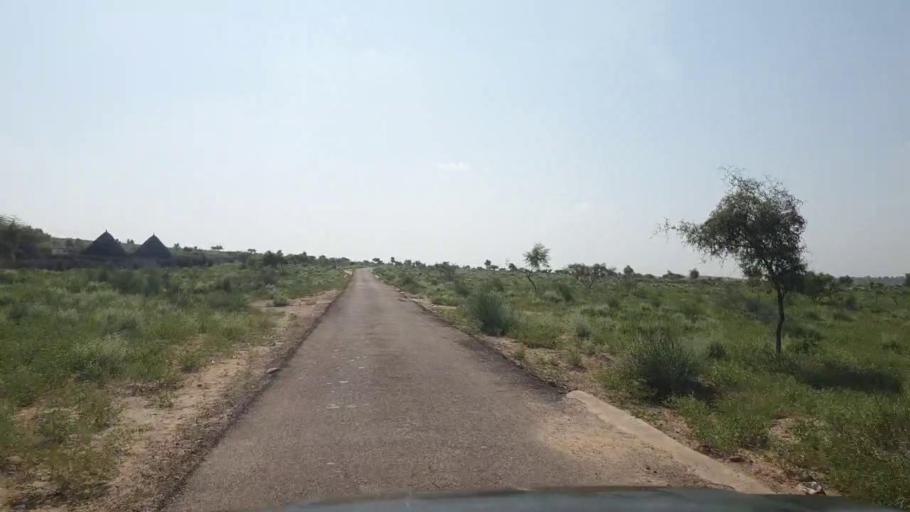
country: PK
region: Sindh
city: Islamkot
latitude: 25.1791
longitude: 70.3940
